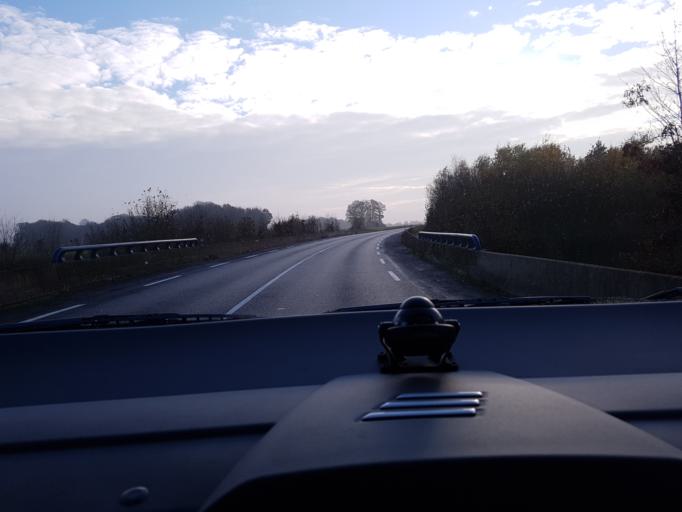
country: FR
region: Lower Normandy
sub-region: Departement de l'Orne
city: La Ferte-Mace
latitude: 48.6106
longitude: -0.3413
